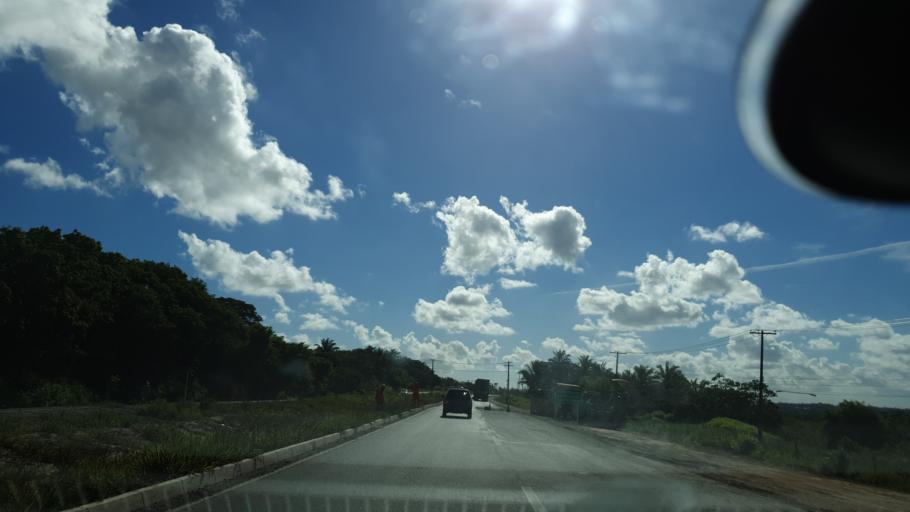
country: BR
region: Bahia
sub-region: Camacari
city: Camacari
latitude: -12.6809
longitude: -38.2863
